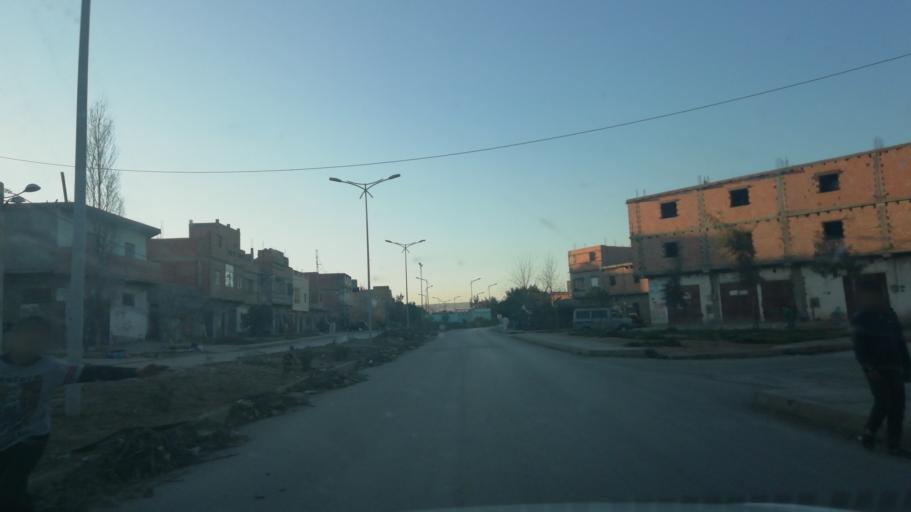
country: DZ
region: Oran
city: Es Senia
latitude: 35.6498
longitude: -0.5762
